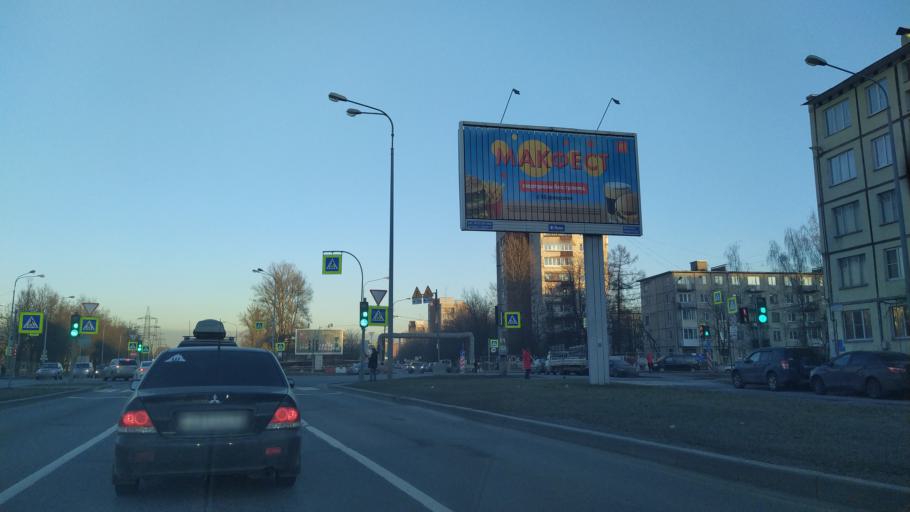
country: RU
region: Leningrad
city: Kalininskiy
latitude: 59.9771
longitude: 30.4010
